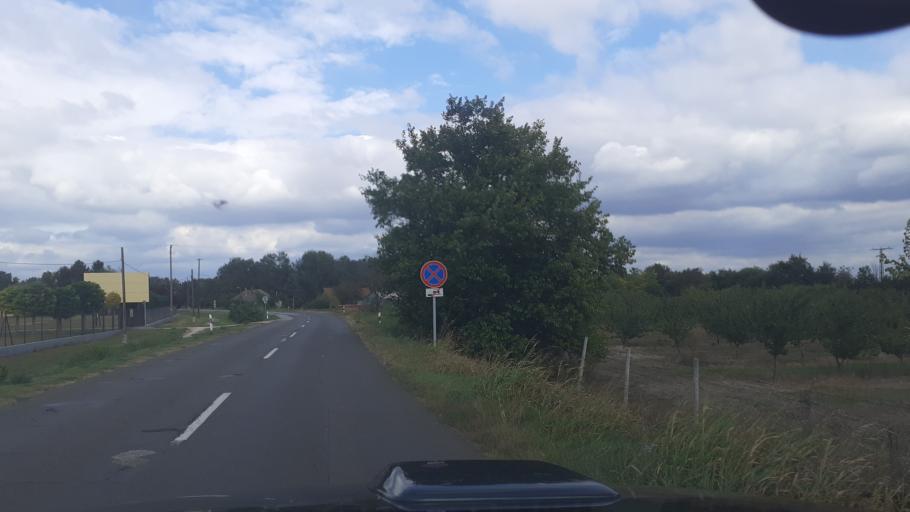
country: HU
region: Bacs-Kiskun
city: Dunavecse
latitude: 46.9227
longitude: 18.9774
